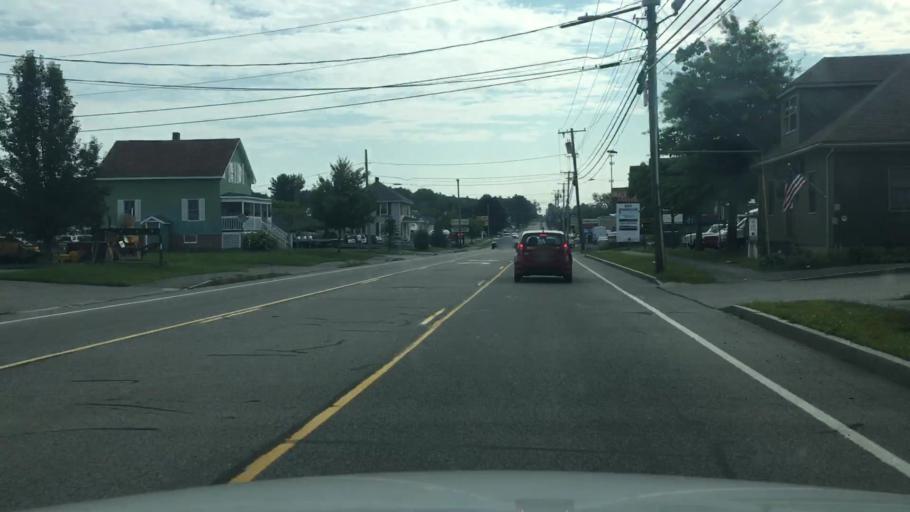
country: US
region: Maine
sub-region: Cumberland County
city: South Portland Gardens
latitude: 43.6873
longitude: -70.3137
